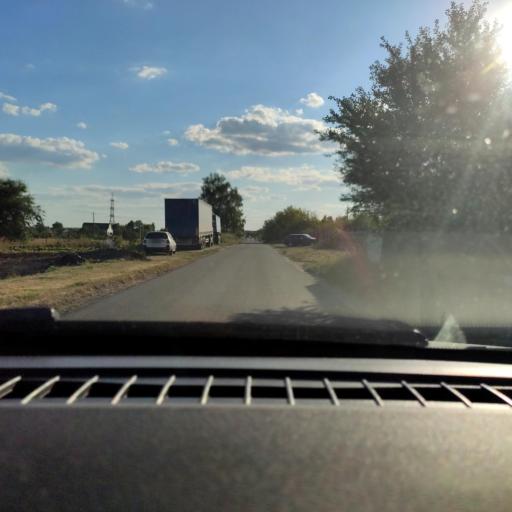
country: RU
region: Voronezj
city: Devitsa
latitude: 51.6469
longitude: 38.9483
